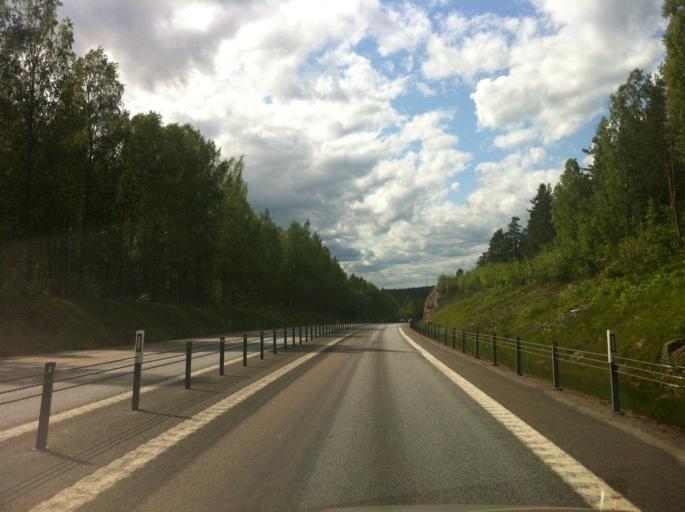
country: SE
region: Vaermland
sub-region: Kristinehamns Kommun
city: Kristinehamn
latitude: 59.3161
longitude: 14.1496
